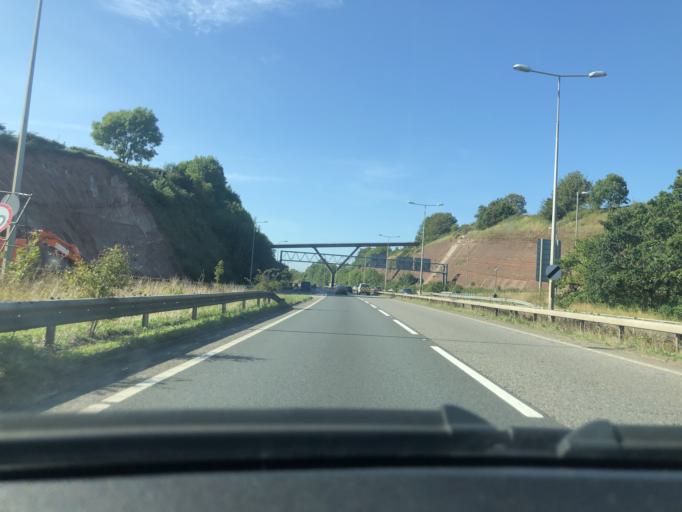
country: GB
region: England
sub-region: Devon
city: Exminster
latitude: 50.6808
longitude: -3.5177
